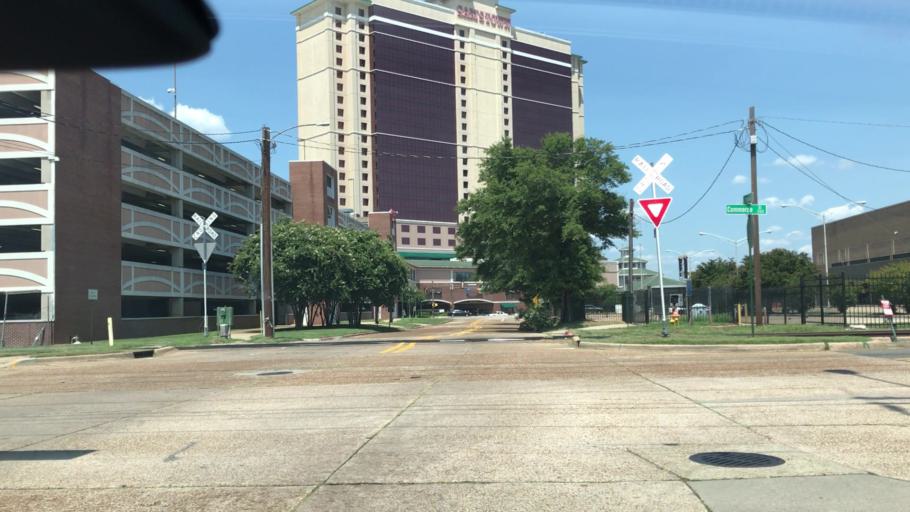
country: US
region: Louisiana
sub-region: Caddo Parish
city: Shreveport
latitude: 32.5173
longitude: -93.7475
